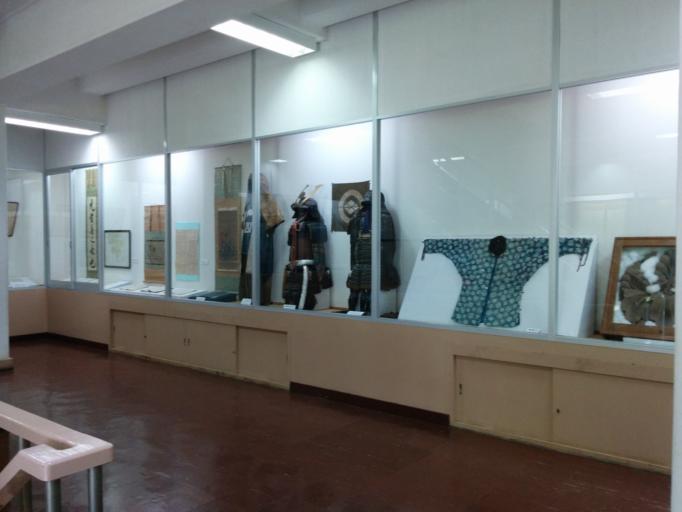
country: JP
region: Hokkaido
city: Kamiiso
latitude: 41.4299
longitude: 140.1087
